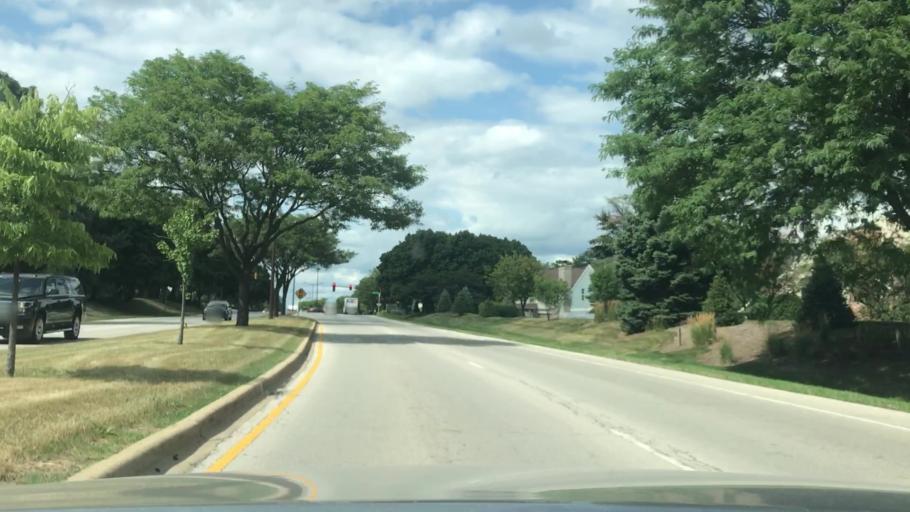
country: US
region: Illinois
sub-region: Kane County
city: Aurora
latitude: 41.7539
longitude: -88.2435
